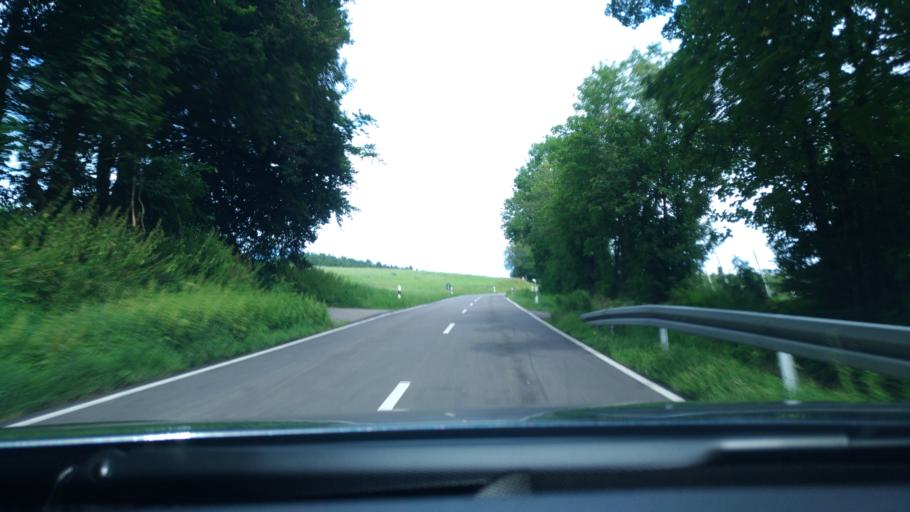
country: DE
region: Baden-Wuerttemberg
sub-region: Freiburg Region
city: Bodman-Ludwigshafen
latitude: 47.8251
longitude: 9.0666
